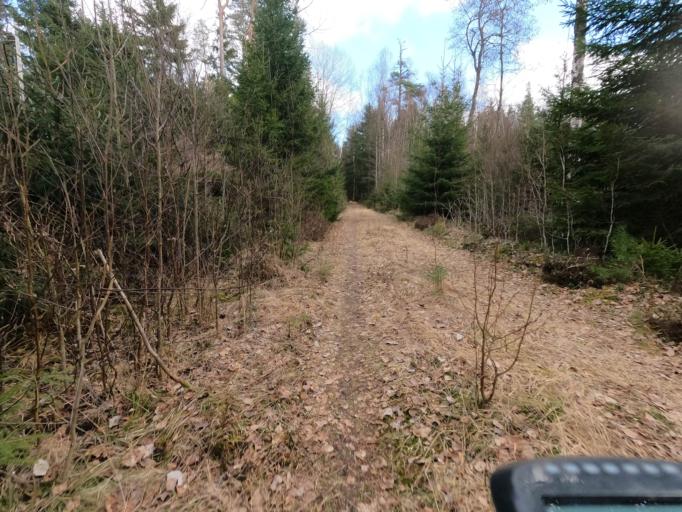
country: SE
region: Joenkoeping
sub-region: Varnamo Kommun
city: Rydaholm
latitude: 56.8238
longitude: 14.2912
